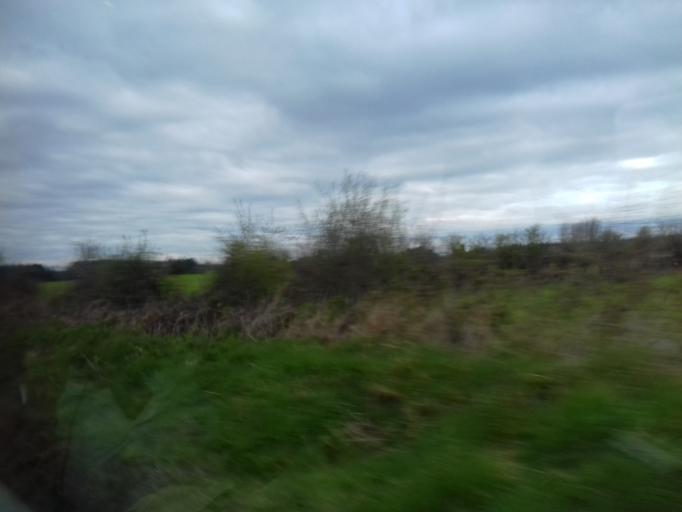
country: IE
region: Leinster
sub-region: An Longfort
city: Granard
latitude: 53.6724
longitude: -7.5134
